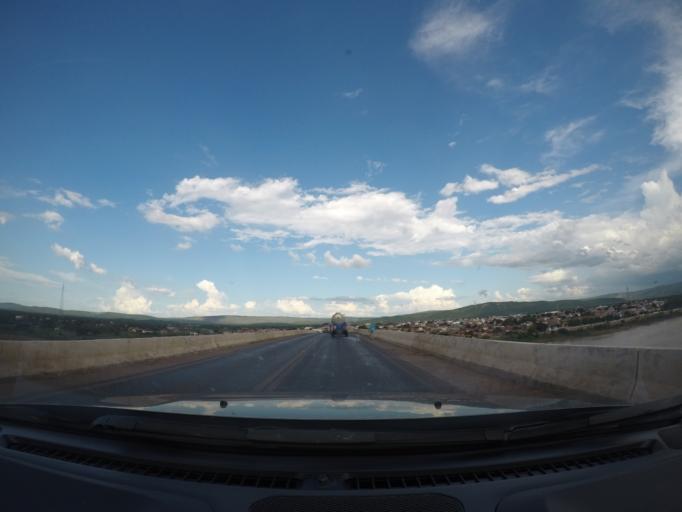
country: BR
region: Bahia
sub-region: Ibotirama
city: Ibotirama
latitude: -12.1804
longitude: -43.2269
